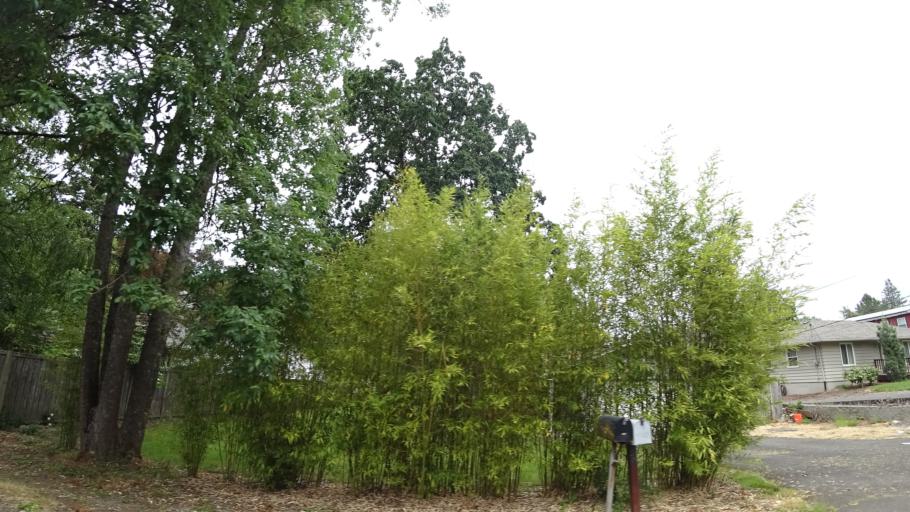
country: US
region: Oregon
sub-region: Washington County
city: Metzger
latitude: 45.4527
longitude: -122.7585
